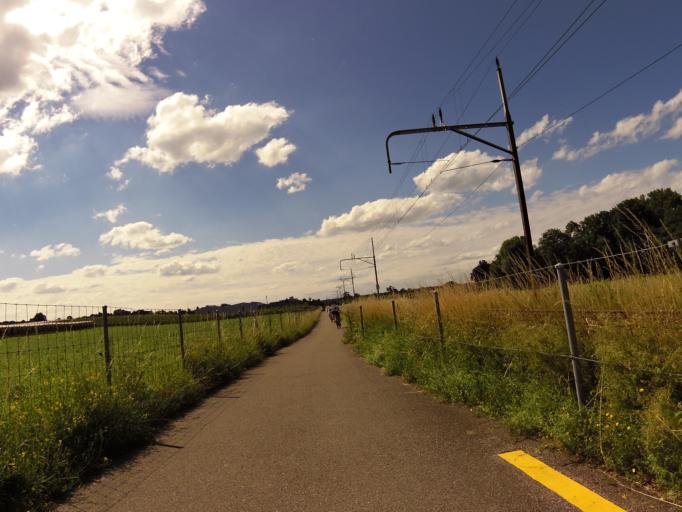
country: CH
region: Thurgau
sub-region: Arbon District
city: Egnach
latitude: 47.5406
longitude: 9.3911
